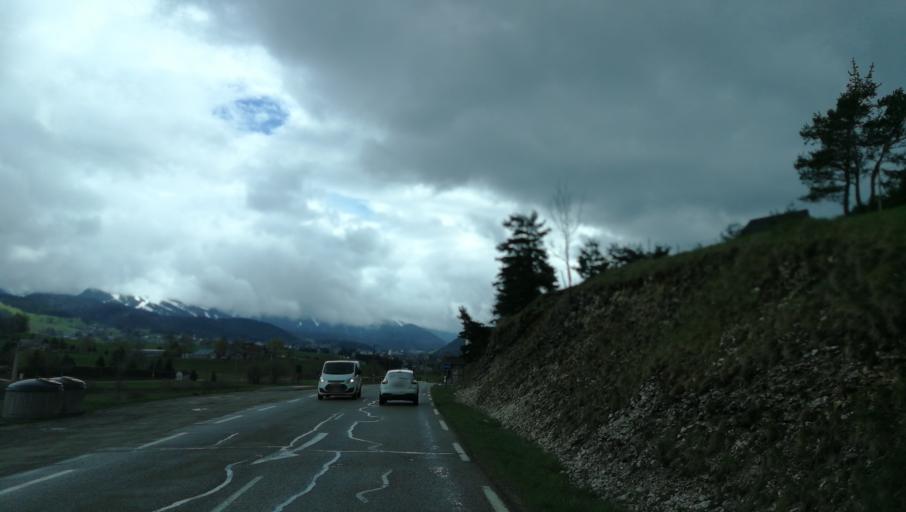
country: FR
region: Rhone-Alpes
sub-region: Departement de l'Isere
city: Villard-de-Lans
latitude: 45.0975
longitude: 5.5574
